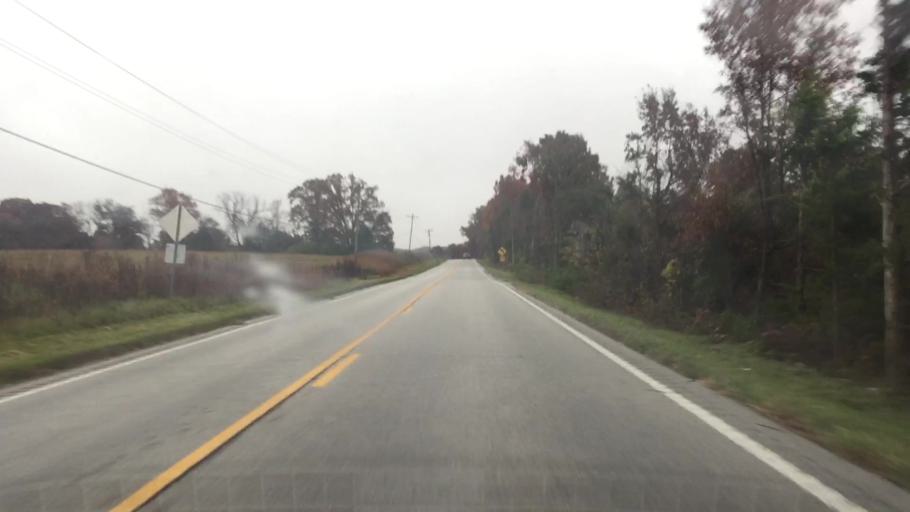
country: US
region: Missouri
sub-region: Callaway County
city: Fulton
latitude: 38.8862
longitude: -92.0959
